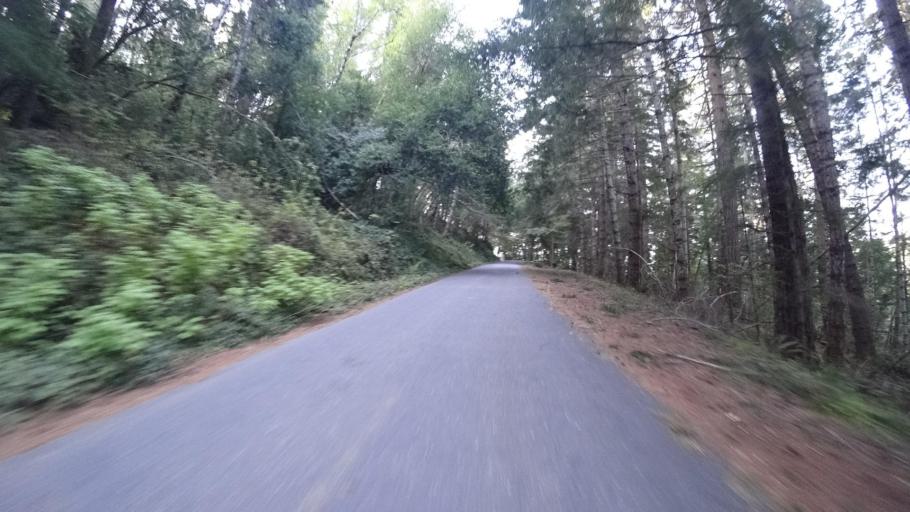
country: US
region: California
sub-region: Humboldt County
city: Bayside
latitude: 40.6939
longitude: -123.9420
